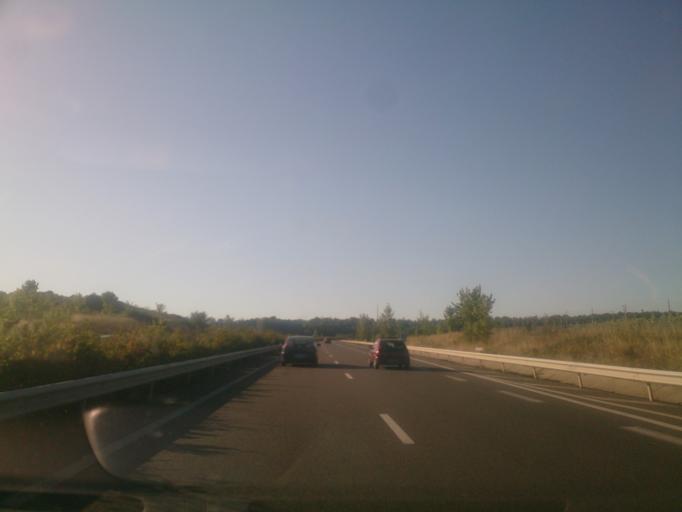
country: FR
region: Midi-Pyrenees
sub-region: Departement du Tarn-et-Garonne
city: Caussade
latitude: 44.2435
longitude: 1.5181
